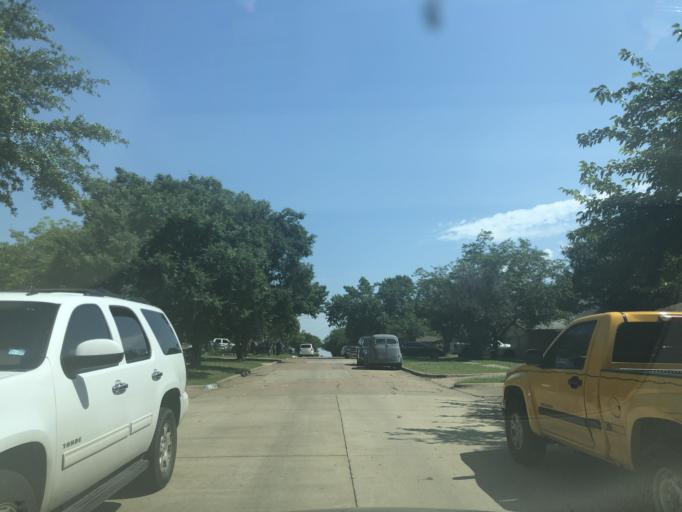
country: US
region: Texas
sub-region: Dallas County
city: Grand Prairie
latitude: 32.7324
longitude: -97.0014
